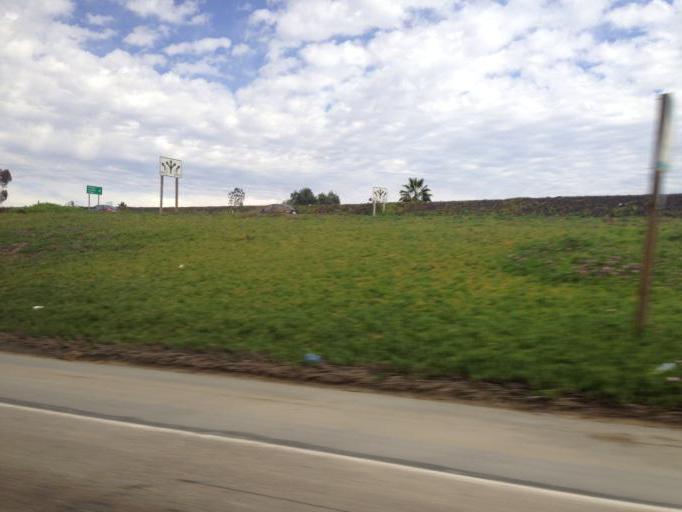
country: US
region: California
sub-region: San Diego County
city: Bonita
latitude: 32.6045
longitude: -117.0362
